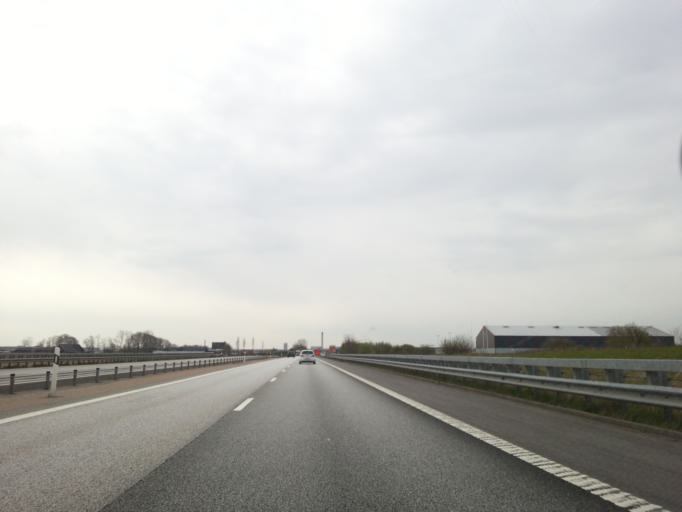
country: SE
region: Skane
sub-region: Angelholms Kommun
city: AEngelholm
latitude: 56.2602
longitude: 12.8955
